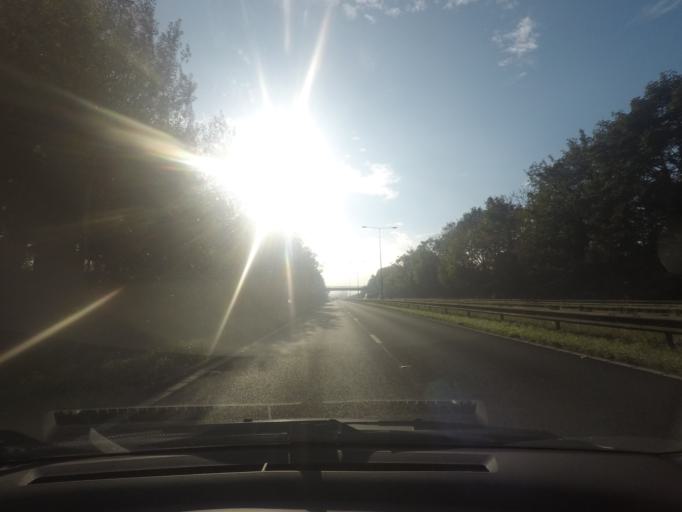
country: GB
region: England
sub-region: East Riding of Yorkshire
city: Brough
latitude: 53.7414
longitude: -0.5650
